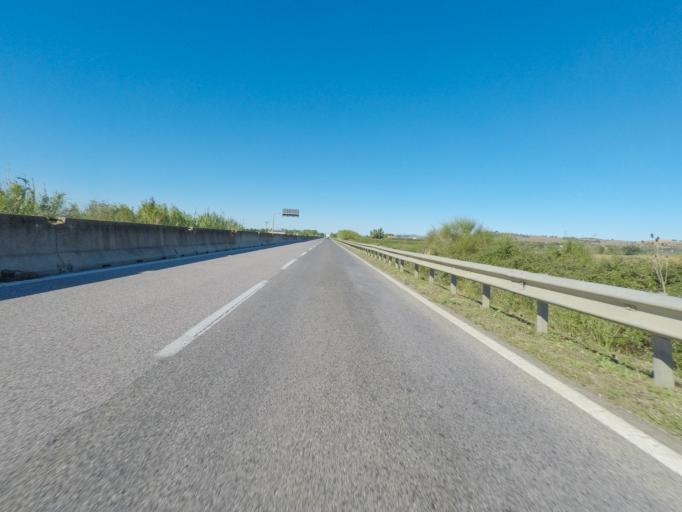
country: IT
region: Tuscany
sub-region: Provincia di Grosseto
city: Grosseto
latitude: 42.6807
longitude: 11.1402
